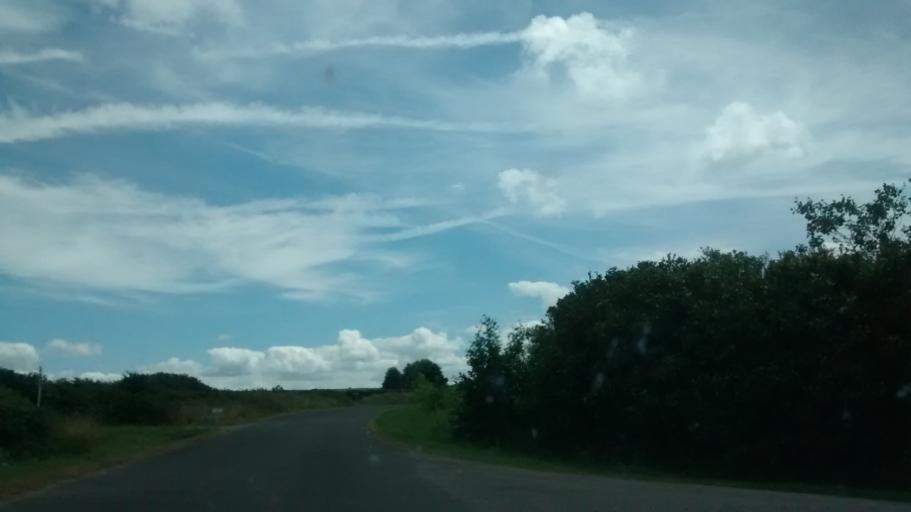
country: FR
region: Brittany
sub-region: Departement du Finistere
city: Plouguerneau
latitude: 48.6218
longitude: -4.4707
